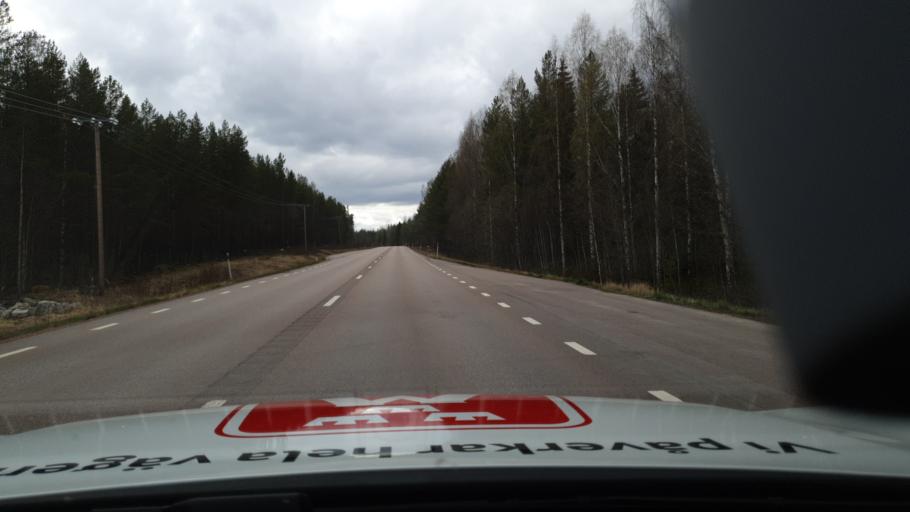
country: SE
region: Jaemtland
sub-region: Ragunda Kommun
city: Hammarstrand
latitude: 63.1733
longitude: 15.8692
